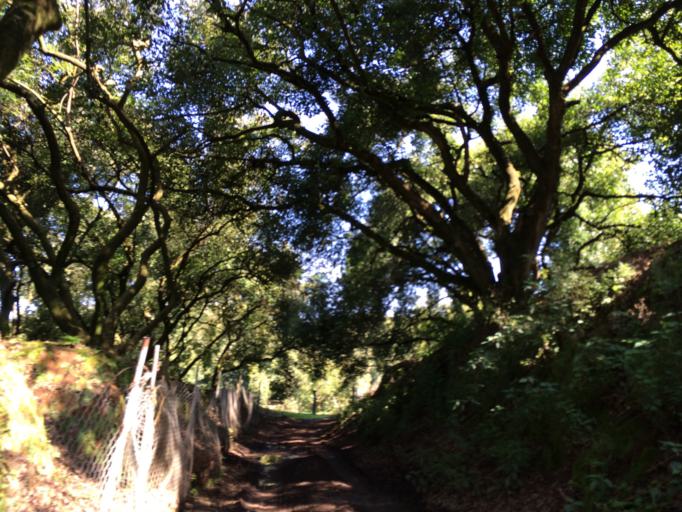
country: MX
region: Michoacan
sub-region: Uruapan
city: Nuevo Zirosto
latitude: 19.5562
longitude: -102.3505
